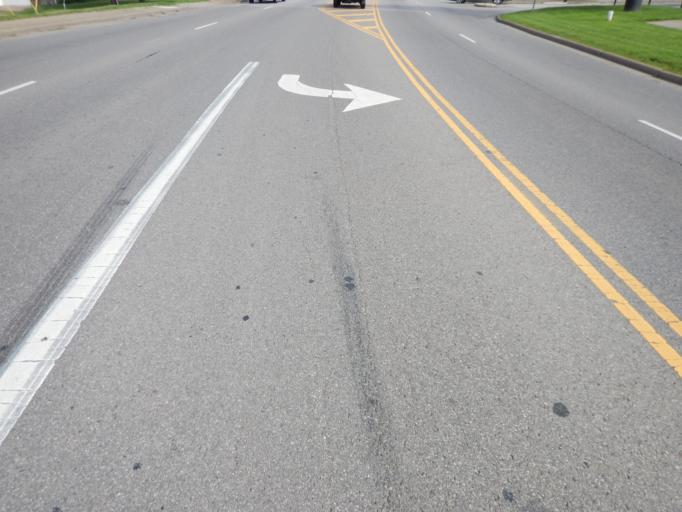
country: US
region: Ohio
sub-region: Muskingum County
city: North Zanesville
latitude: 39.9764
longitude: -82.0151
